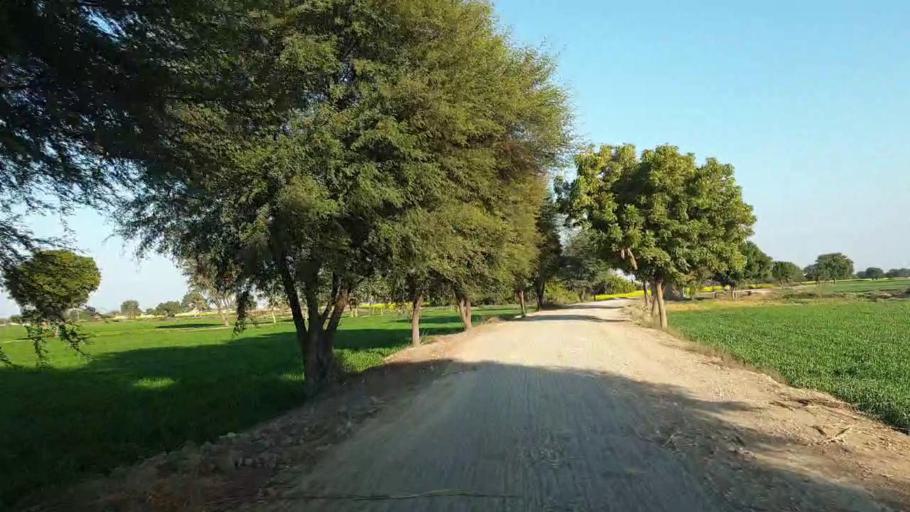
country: PK
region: Sindh
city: Shahpur Chakar
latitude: 26.1285
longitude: 68.5513
